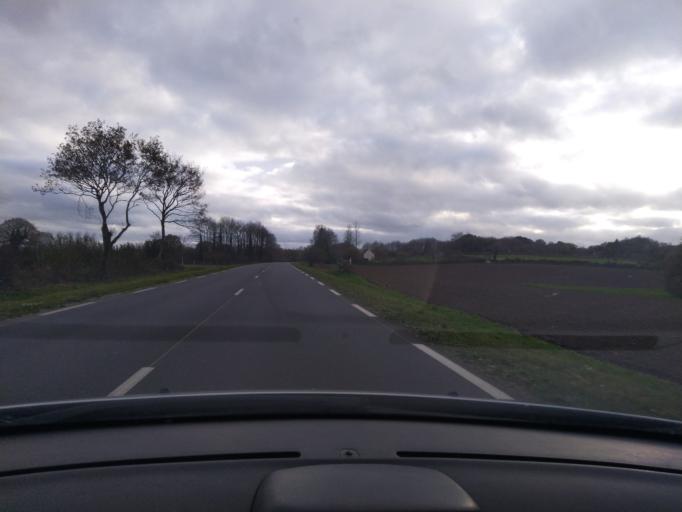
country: FR
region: Brittany
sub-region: Departement des Cotes-d'Armor
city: Plounevez-Moedec
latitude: 48.5706
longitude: -3.4949
